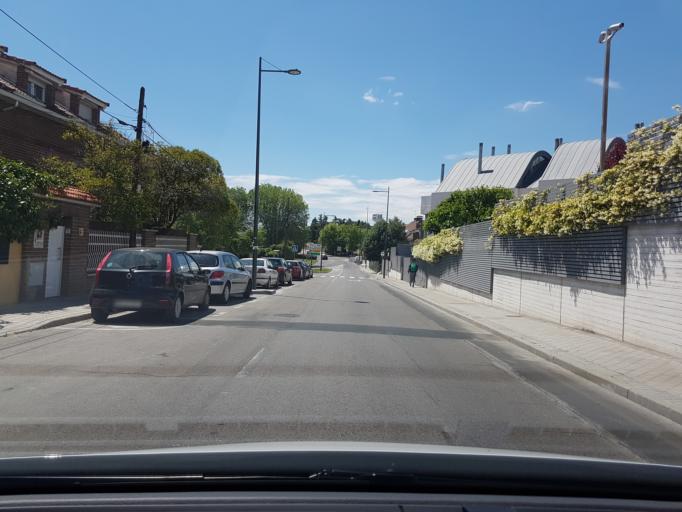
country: ES
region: Madrid
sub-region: Provincia de Madrid
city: Pozuelo de Alarcon
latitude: 40.4322
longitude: -3.8113
